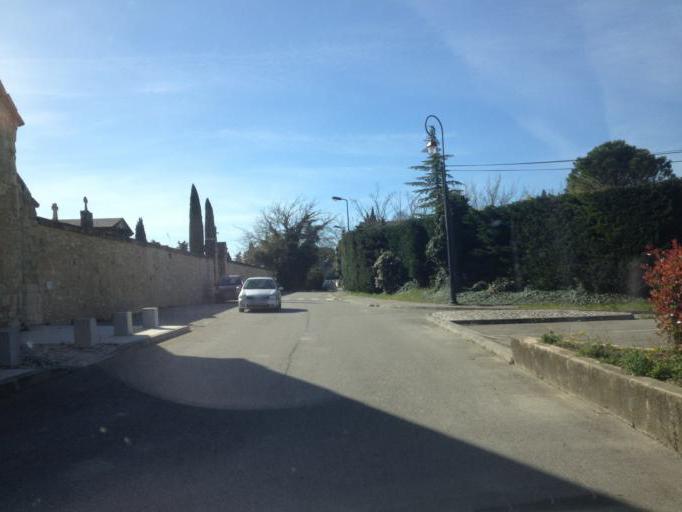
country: FR
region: Provence-Alpes-Cote d'Azur
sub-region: Departement du Vaucluse
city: Caderousse
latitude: 44.1076
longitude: 4.7549
